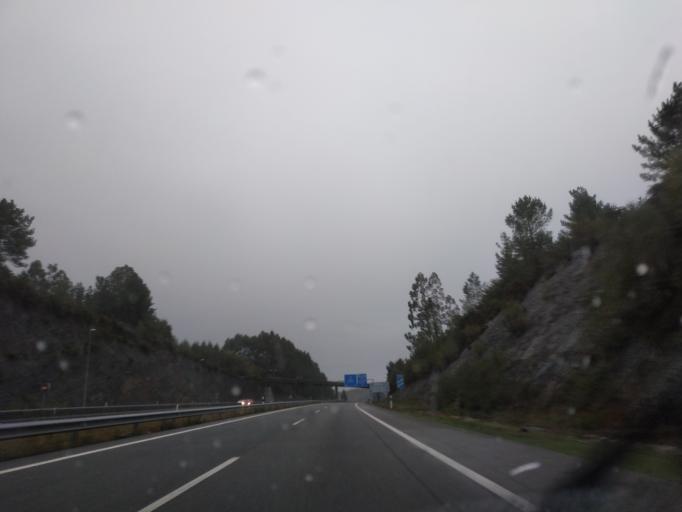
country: ES
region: Galicia
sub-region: Provincia de Lugo
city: Begonte
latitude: 43.1775
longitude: -7.7609
